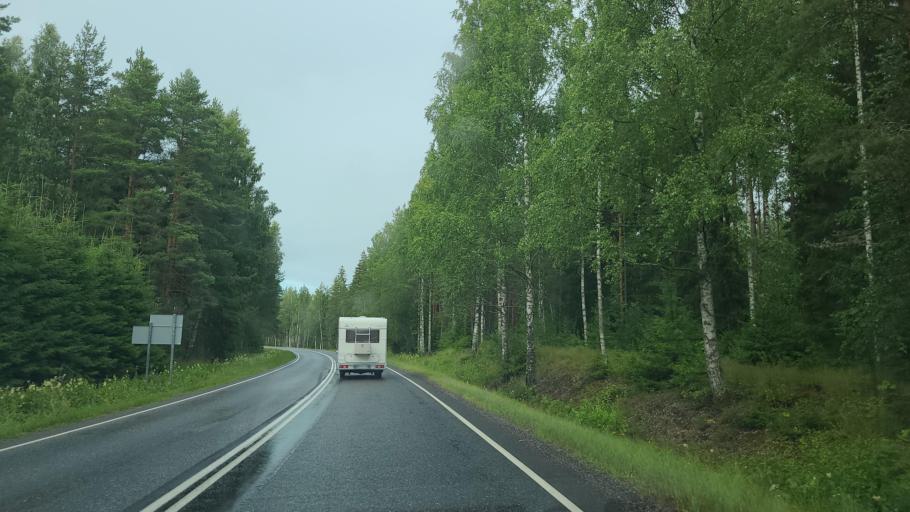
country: FI
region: Varsinais-Suomi
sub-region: Turku
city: Sauvo
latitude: 60.3235
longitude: 22.7120
